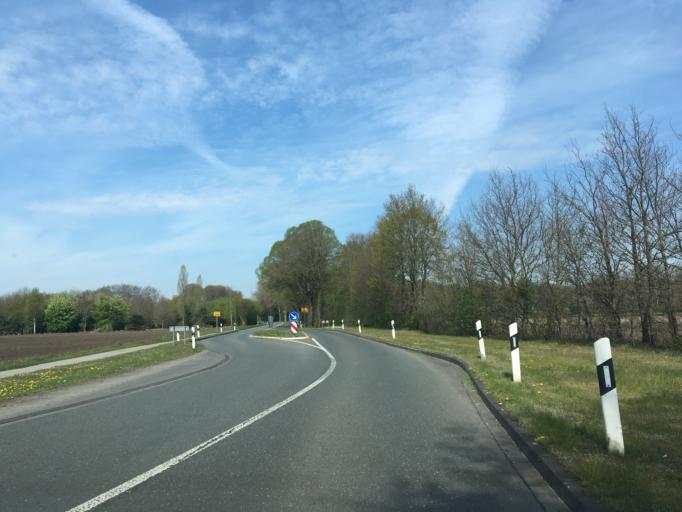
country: DE
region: North Rhine-Westphalia
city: Stadtlohn
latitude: 52.0017
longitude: 6.8777
